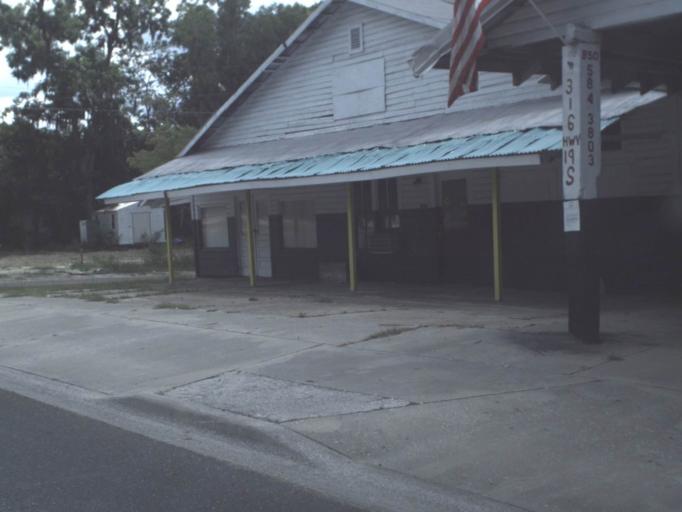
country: US
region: Florida
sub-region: Taylor County
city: Perry
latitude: 30.1146
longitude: -83.5893
